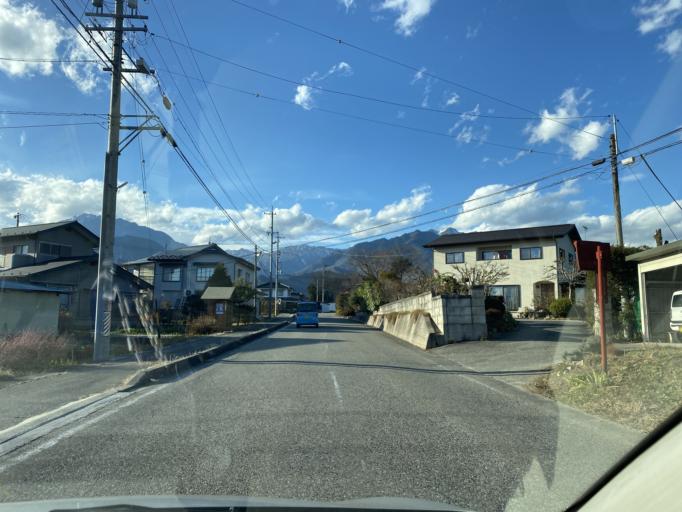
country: JP
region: Nagano
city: Omachi
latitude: 36.5246
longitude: 137.8296
